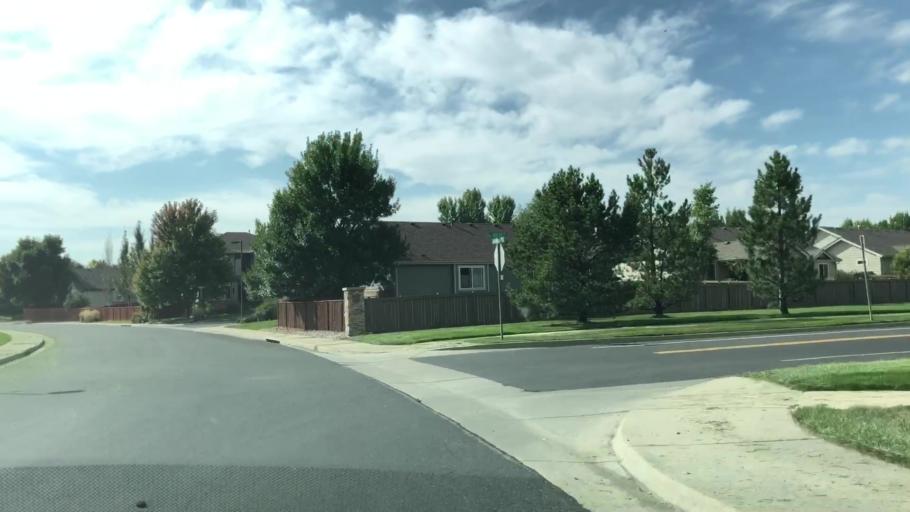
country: US
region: Colorado
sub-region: Larimer County
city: Loveland
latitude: 40.4318
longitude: -105.0566
